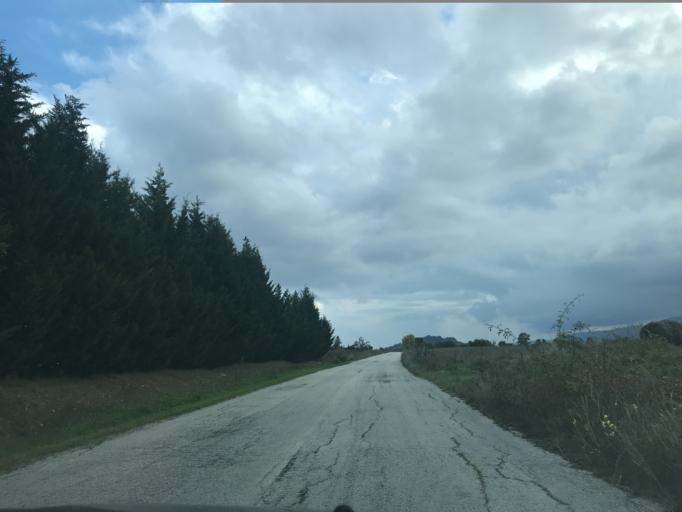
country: IT
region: Molise
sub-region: Provincia di Isernia
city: Bagnoli del Trigno
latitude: 41.6914
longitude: 14.4621
